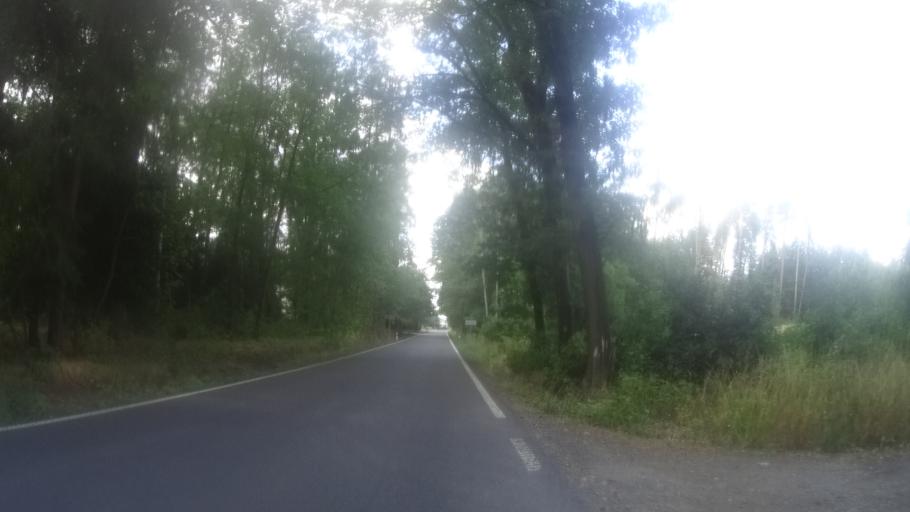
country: CZ
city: Borohradek
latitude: 50.0905
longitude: 16.1043
